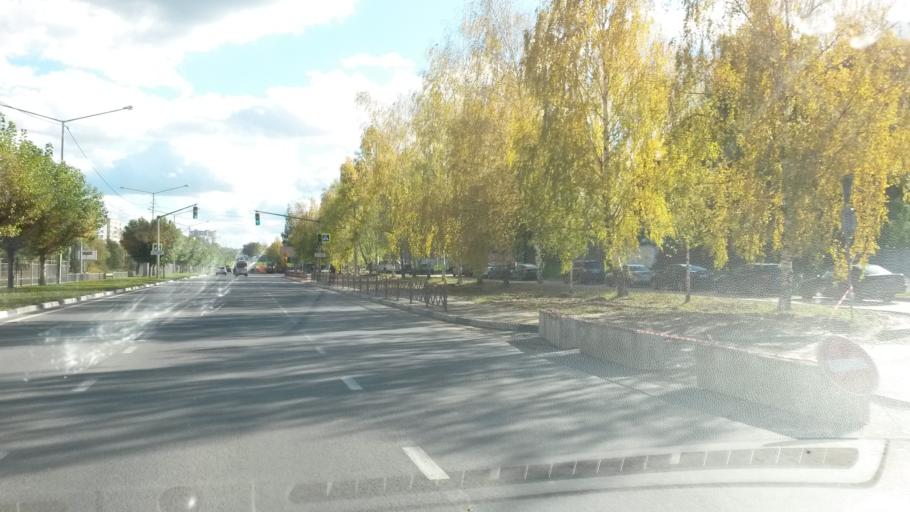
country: RU
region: Jaroslavl
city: Yaroslavl
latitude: 57.5781
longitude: 39.9146
